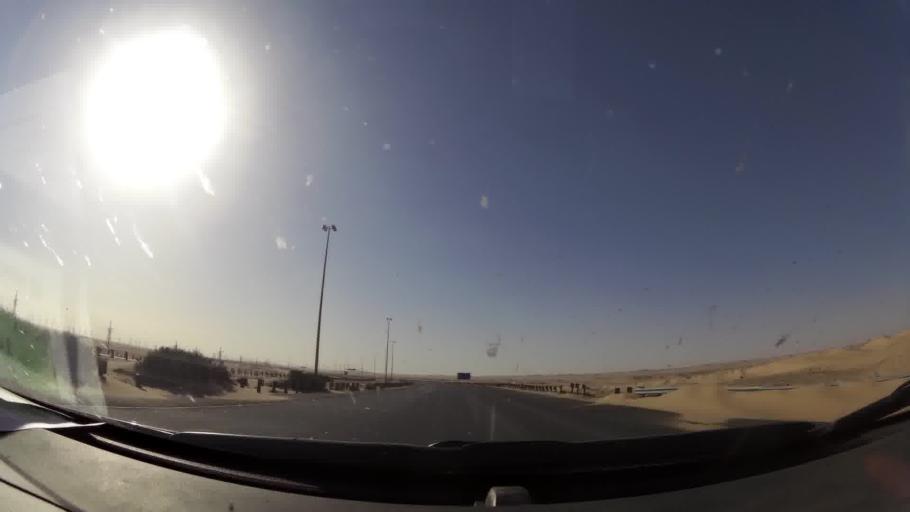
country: KW
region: Al Asimah
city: Kuwait City
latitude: 29.6446
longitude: 47.9484
